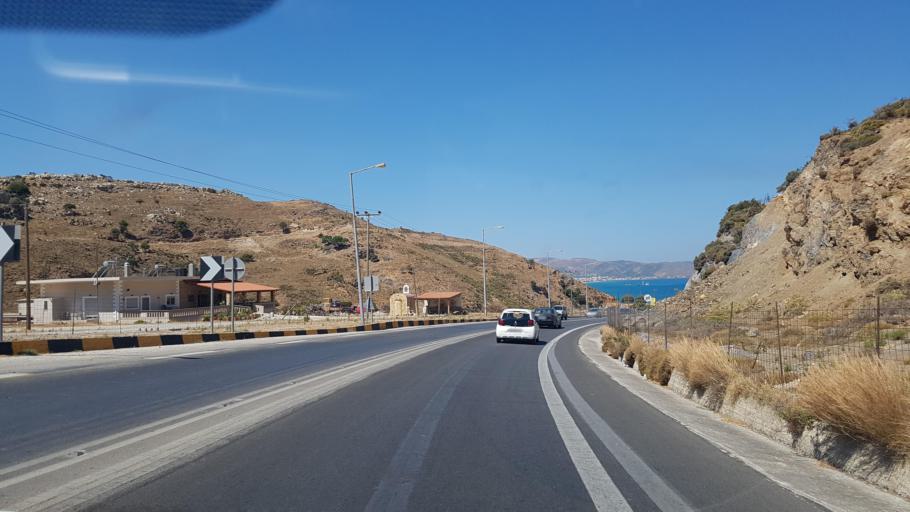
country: GR
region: Crete
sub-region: Nomos Chanias
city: Kolympari
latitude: 35.5084
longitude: 23.7293
